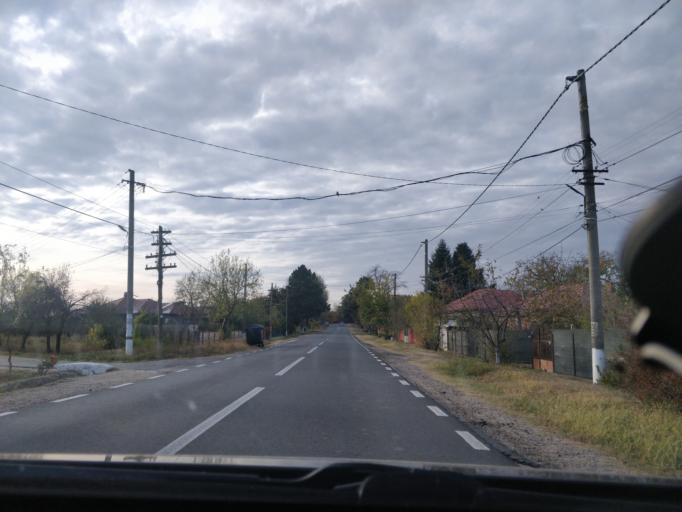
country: RO
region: Giurgiu
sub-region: Comuna Bucsani
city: Bucsani
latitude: 44.3672
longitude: 25.6643
